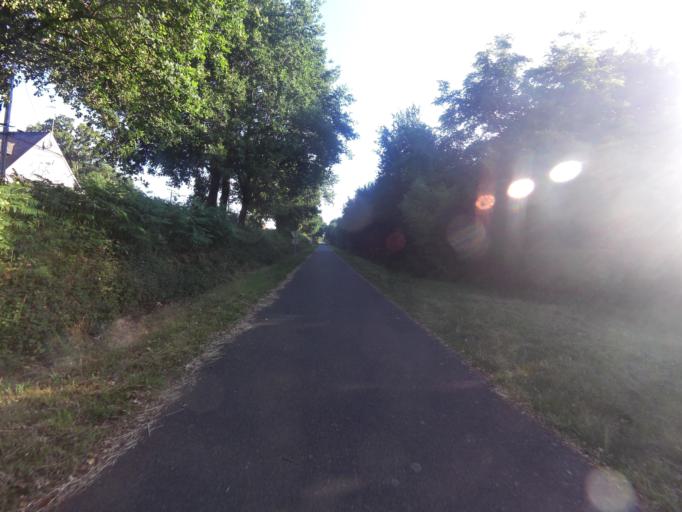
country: FR
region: Brittany
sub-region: Departement du Morbihan
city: Guillac
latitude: 47.8586
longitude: -2.4395
